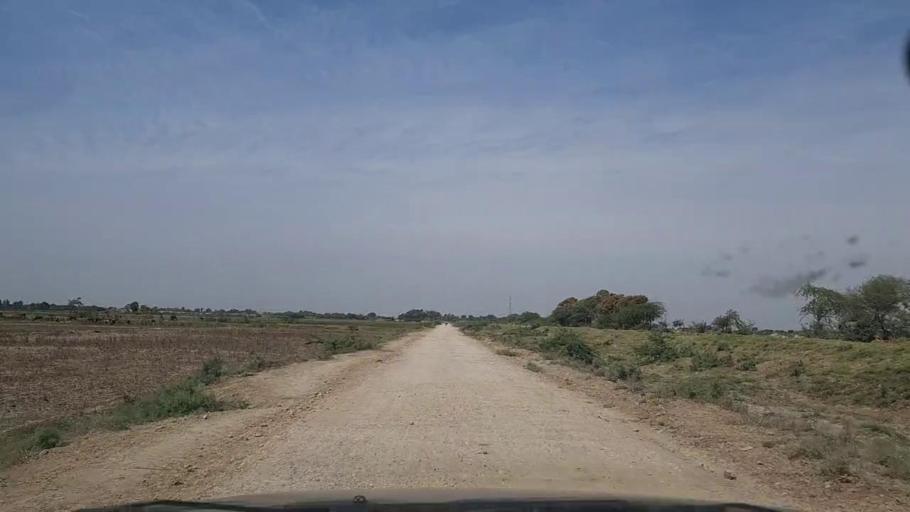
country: PK
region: Sindh
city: Mirpur Batoro
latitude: 24.6491
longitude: 68.1855
